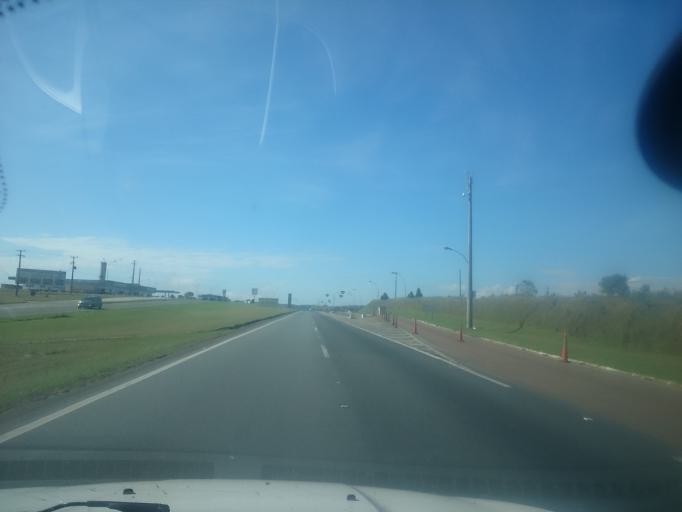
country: BR
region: Parana
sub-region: Campo Largo
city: Campo Largo
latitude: -25.4745
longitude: -49.7047
